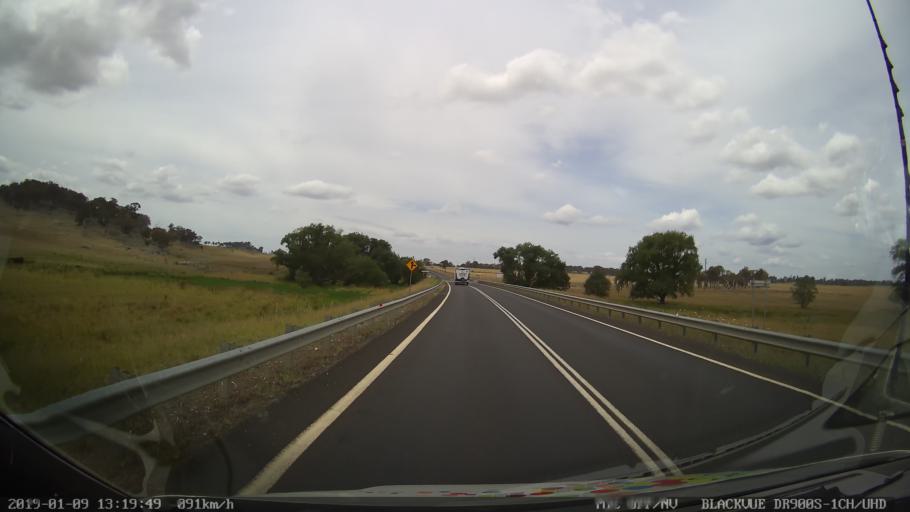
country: AU
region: New South Wales
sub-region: Armidale Dumaresq
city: Armidale
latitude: -30.5380
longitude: 151.8408
